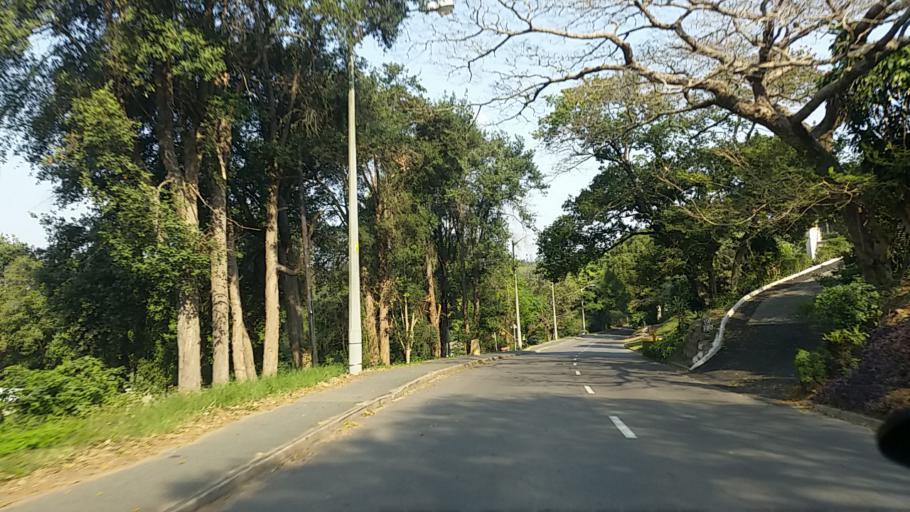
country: ZA
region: KwaZulu-Natal
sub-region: eThekwini Metropolitan Municipality
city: Berea
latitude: -29.8348
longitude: 30.9410
